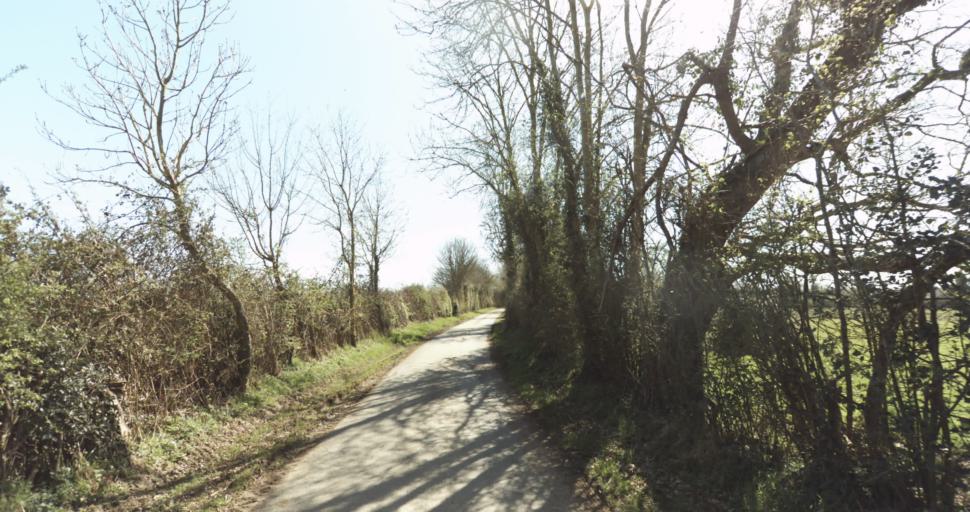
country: FR
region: Lower Normandy
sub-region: Departement du Calvados
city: Livarot
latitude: 49.0218
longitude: 0.1013
